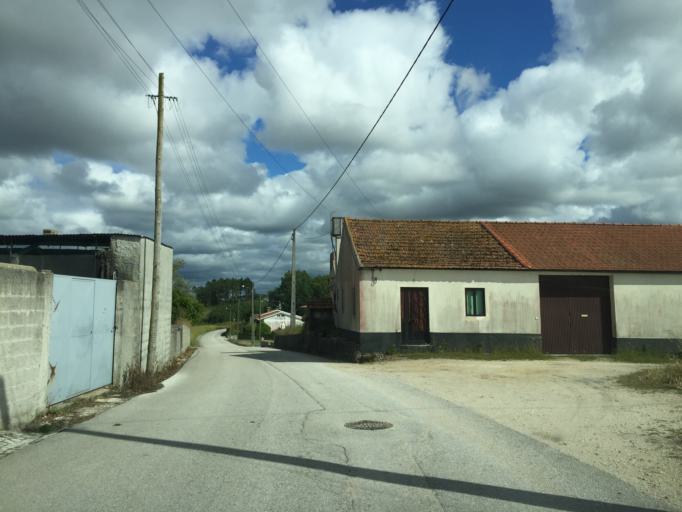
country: PT
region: Leiria
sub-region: Pombal
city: Lourical
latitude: 39.9817
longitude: -8.8060
